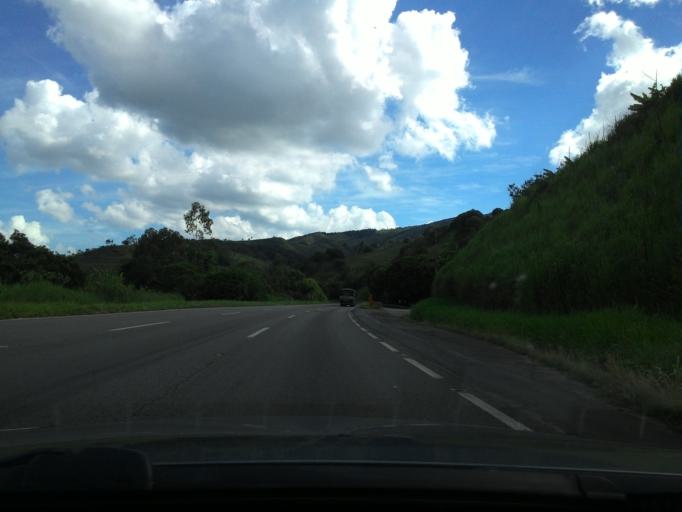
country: BR
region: Sao Paulo
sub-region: Cajati
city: Cajati
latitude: -24.8038
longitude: -48.2138
